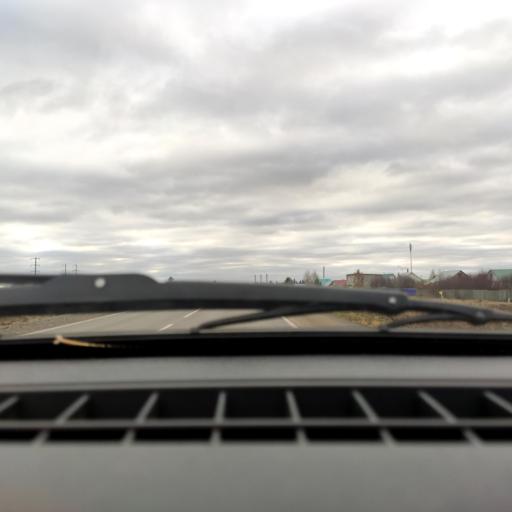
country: RU
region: Bashkortostan
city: Iglino
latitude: 54.7816
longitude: 56.2530
